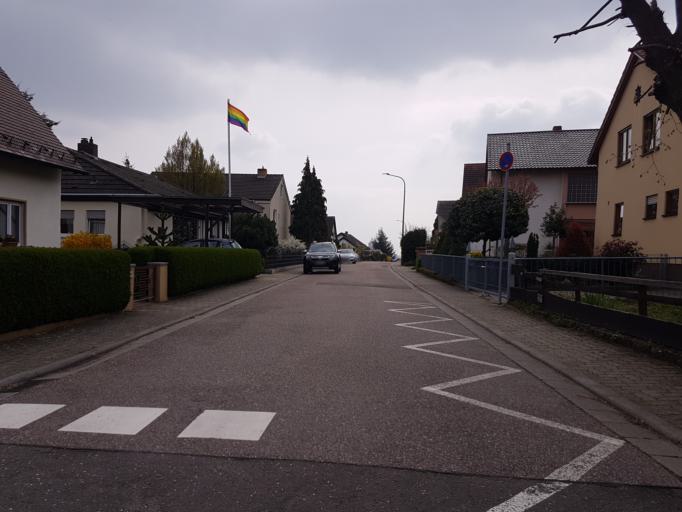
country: DE
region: Rheinland-Pfalz
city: Gleisweiler
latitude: 49.2395
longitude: 8.0643
